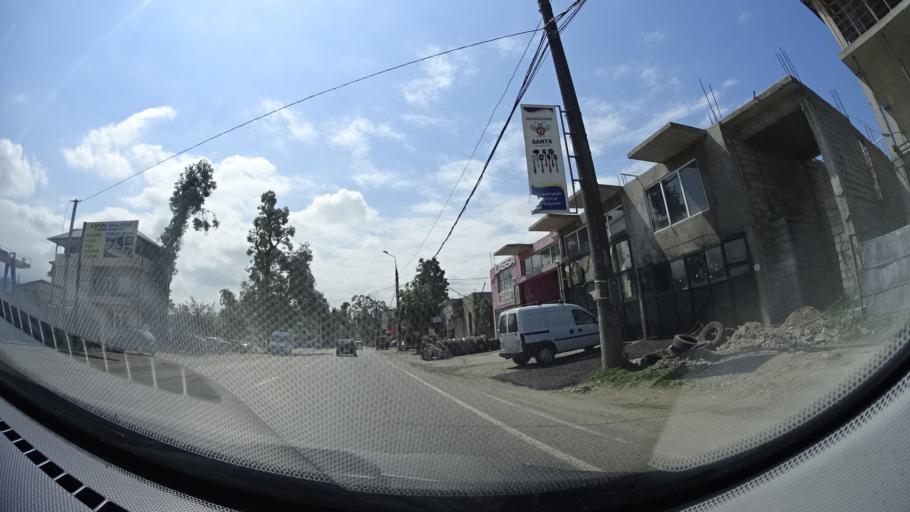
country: GE
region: Ajaria
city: Batumi
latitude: 41.6177
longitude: 41.6189
